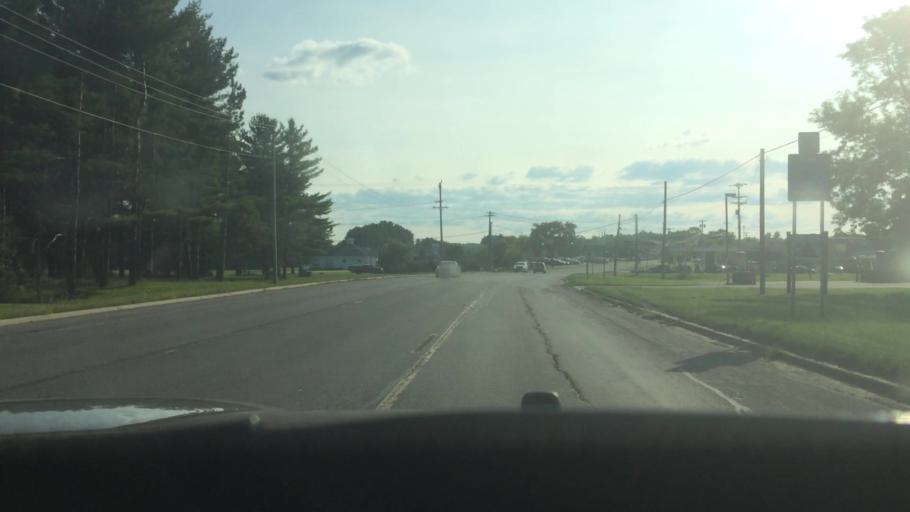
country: US
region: New York
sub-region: St. Lawrence County
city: Canton
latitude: 44.5981
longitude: -75.1458
